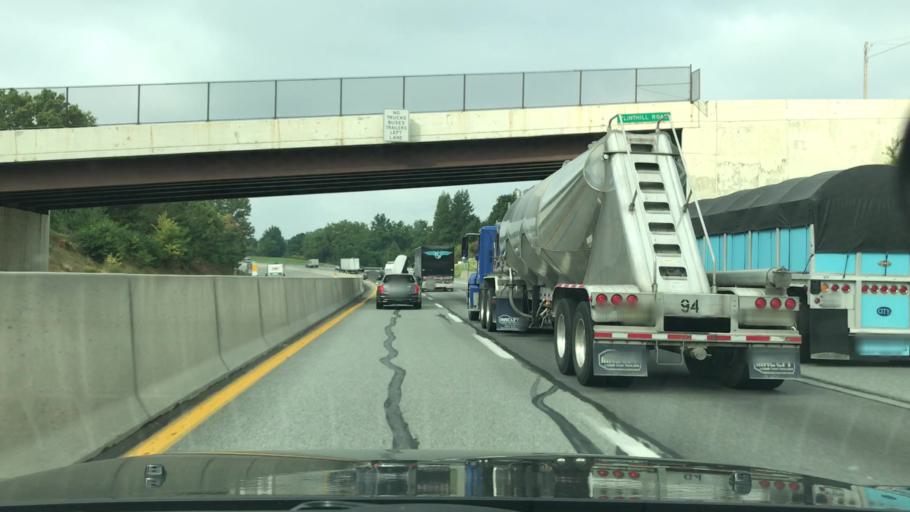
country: US
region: Pennsylvania
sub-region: Montgomery County
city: Bridgeport
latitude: 40.0981
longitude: -75.3393
